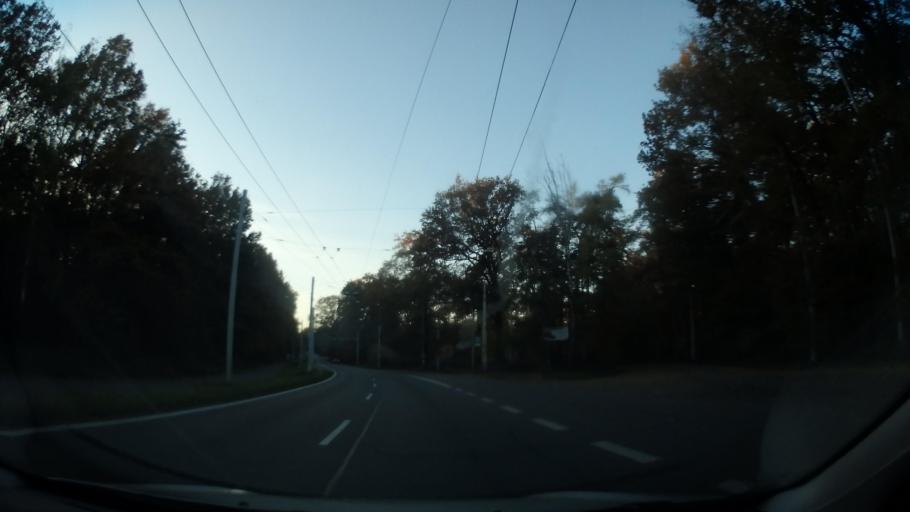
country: CZ
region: Pardubicky
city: Rybitvi
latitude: 50.0651
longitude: 15.7093
